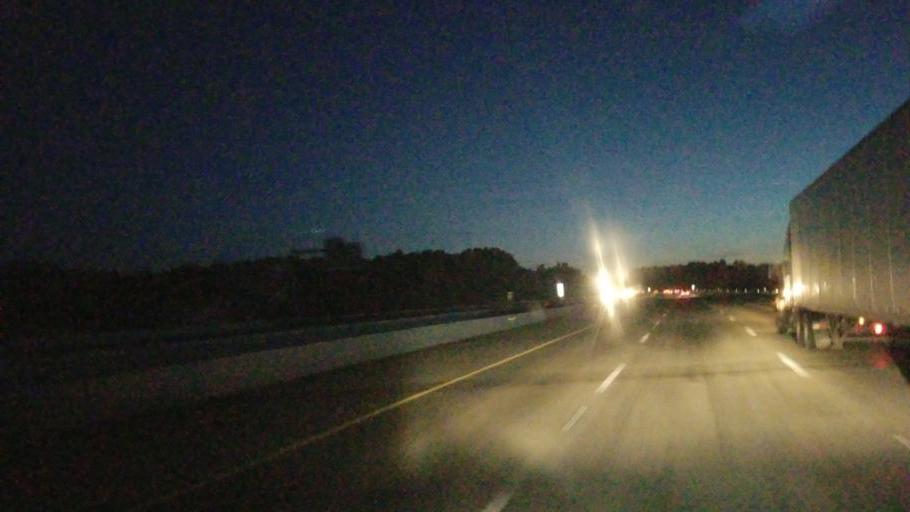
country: US
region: Ohio
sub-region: Richland County
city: Lincoln Heights
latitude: 40.7359
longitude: -82.4632
